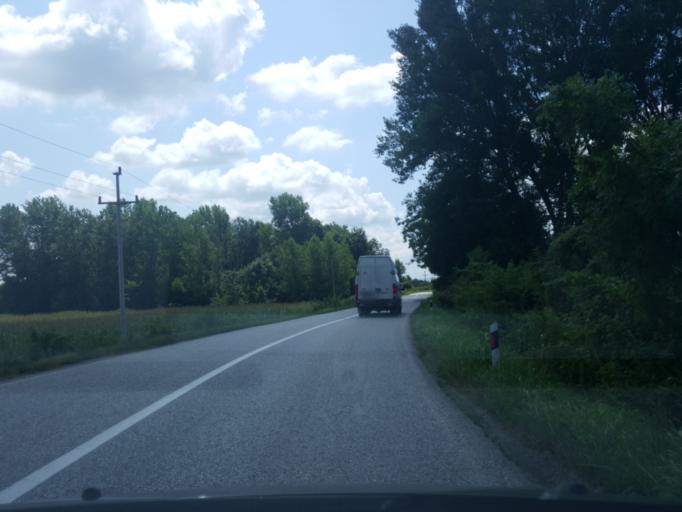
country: RS
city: Glusci
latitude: 44.9045
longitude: 19.5468
